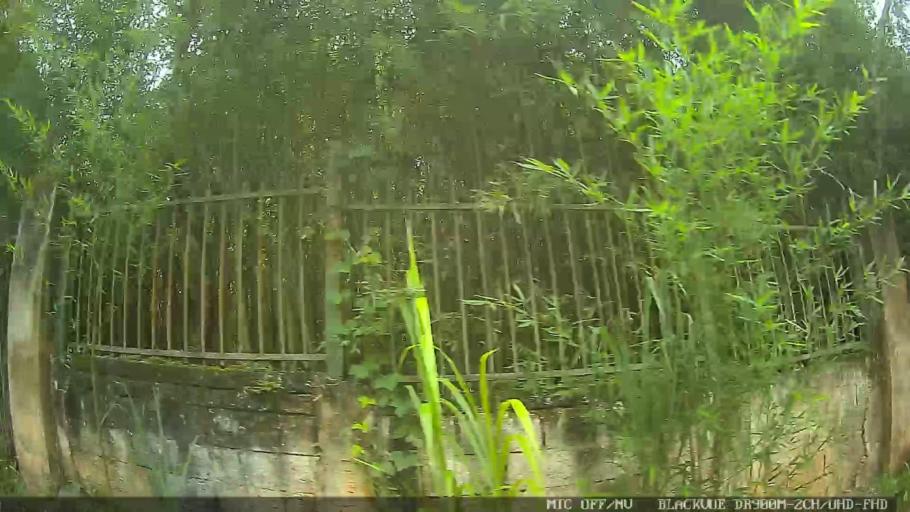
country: BR
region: Sao Paulo
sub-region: Santa Isabel
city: Santa Isabel
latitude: -23.3642
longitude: -46.2474
